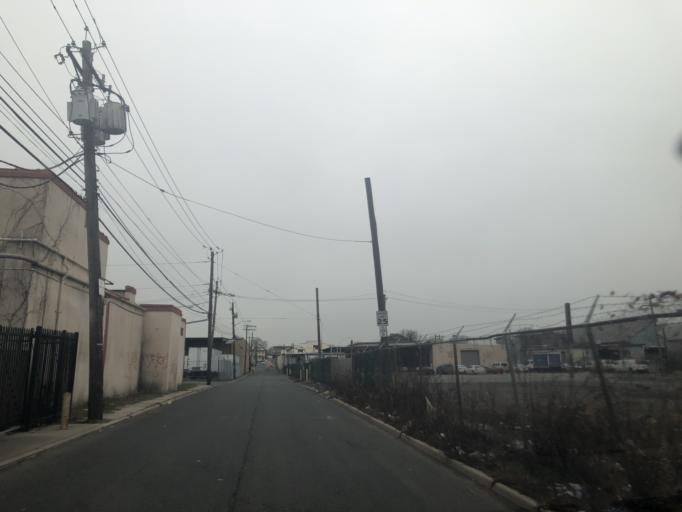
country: US
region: New Jersey
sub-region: Union County
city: Elizabeth
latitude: 40.6736
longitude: -74.1956
